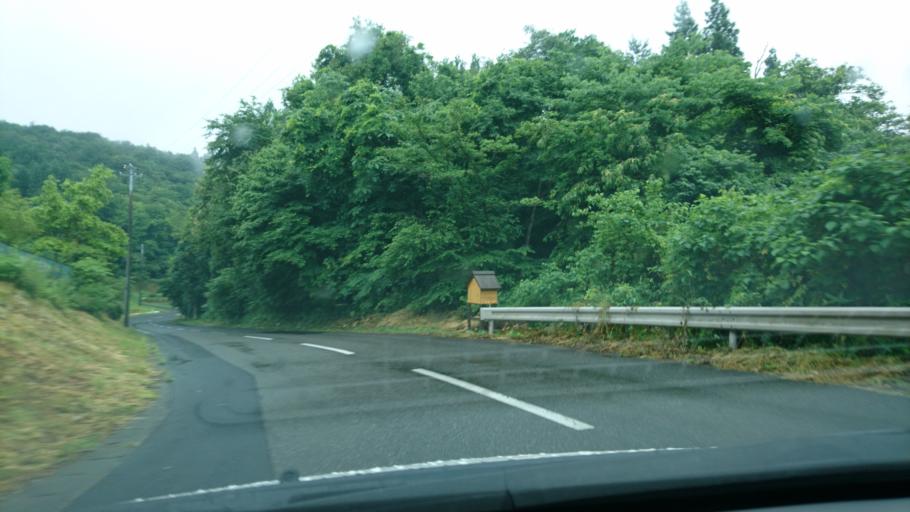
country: JP
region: Iwate
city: Ichinoseki
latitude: 38.9054
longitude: 141.0303
